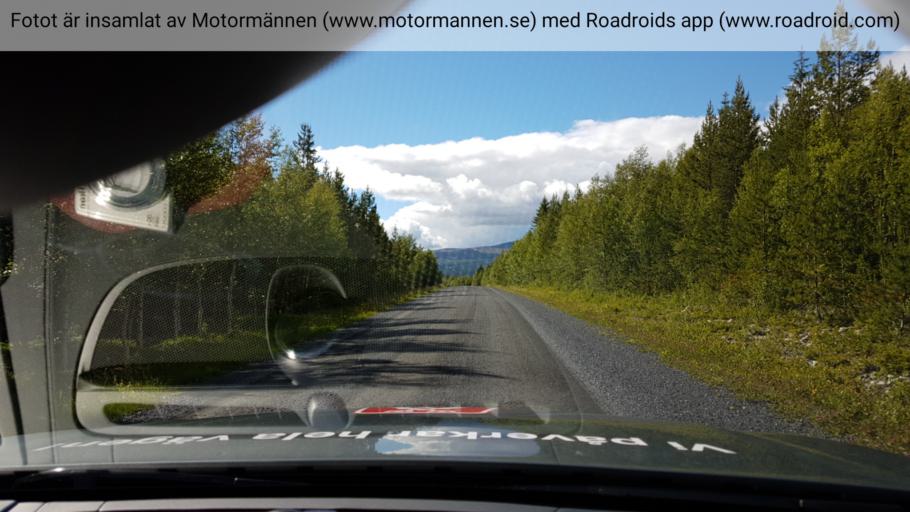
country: SE
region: Jaemtland
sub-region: Krokoms Kommun
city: Valla
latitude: 63.0822
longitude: 13.9291
